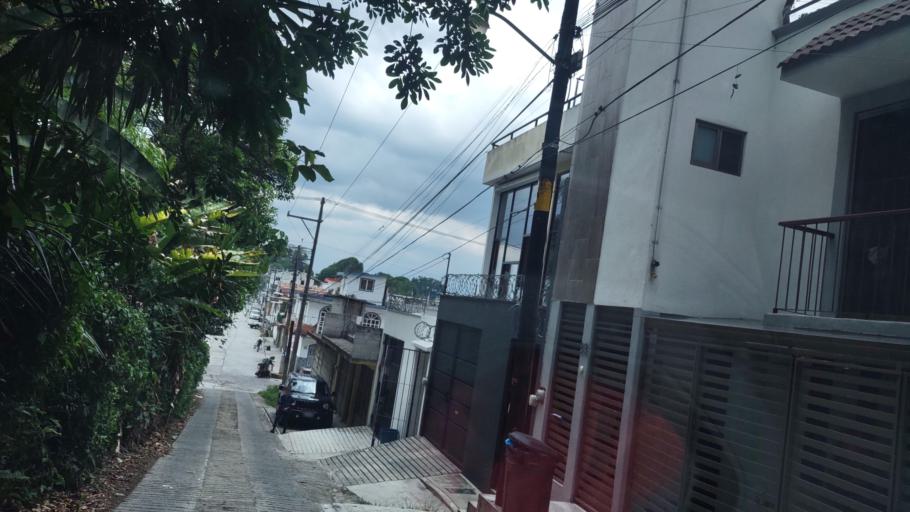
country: MX
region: Veracruz
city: Coatepec
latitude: 19.4605
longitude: -96.9491
